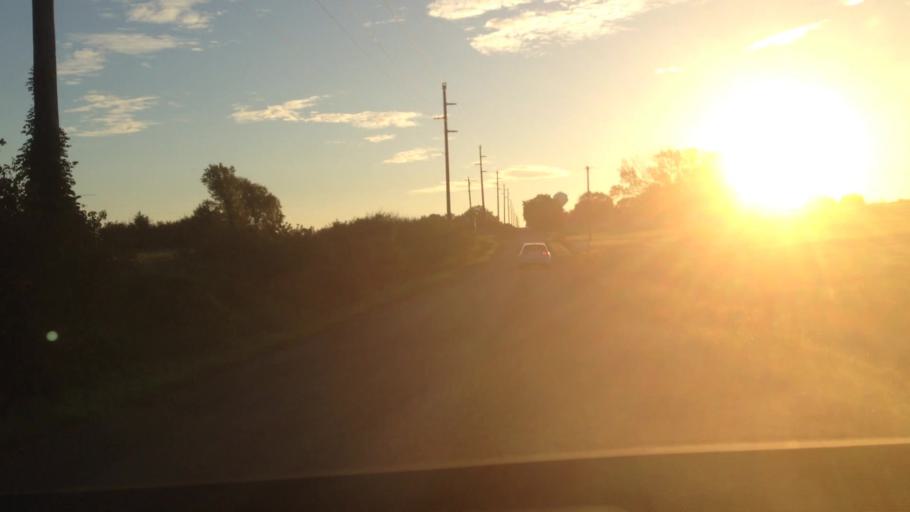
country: US
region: Kansas
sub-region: Johnson County
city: De Soto
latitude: 38.9568
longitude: -95.0128
